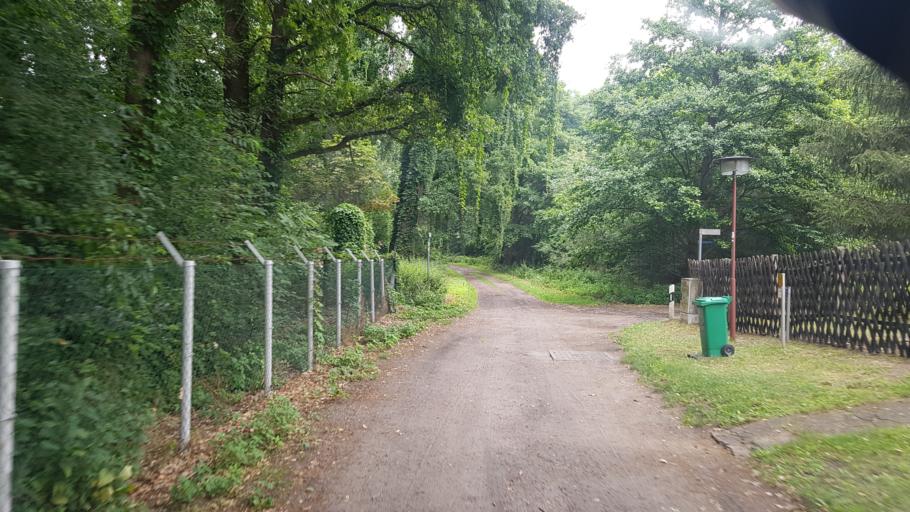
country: DE
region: Brandenburg
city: Gross Koris
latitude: 52.1728
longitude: 13.6992
